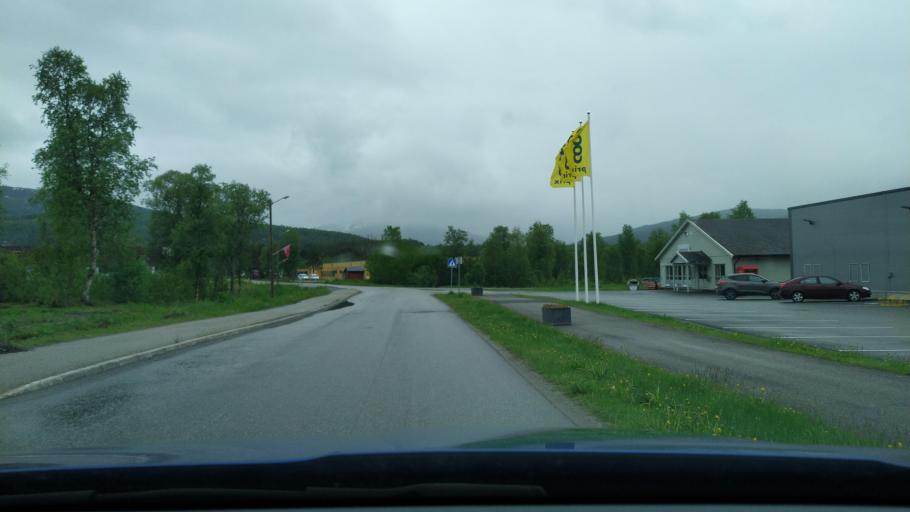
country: NO
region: Troms
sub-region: Dyroy
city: Brostadbotn
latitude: 69.0919
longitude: 17.6951
